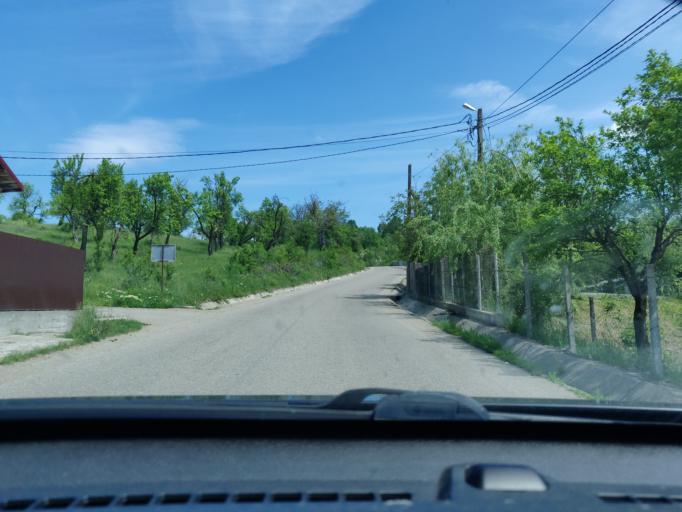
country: RO
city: Vizantea-Manastireasca
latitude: 45.9909
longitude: 26.7757
